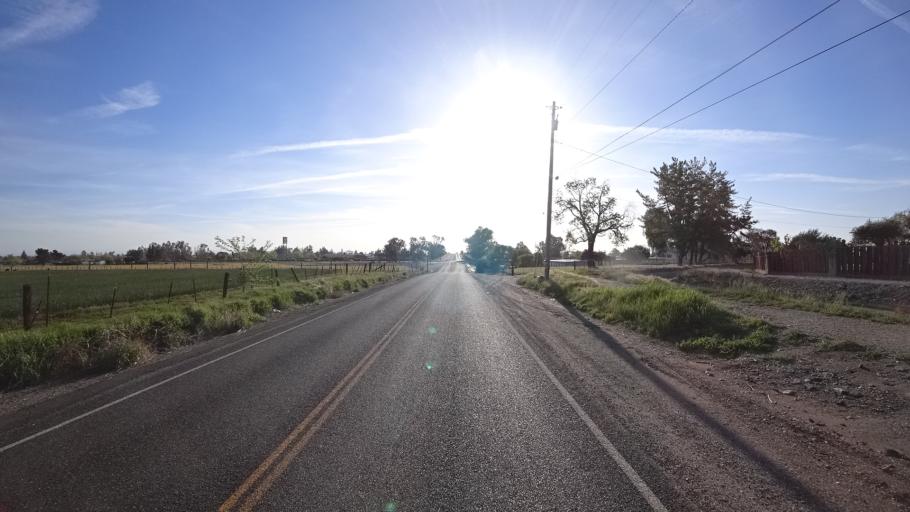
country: US
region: California
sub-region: Glenn County
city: Orland
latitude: 39.7404
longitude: -122.2097
